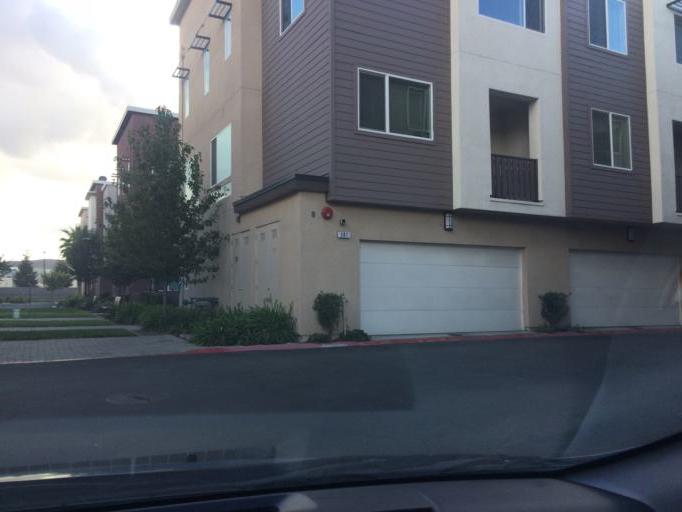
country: US
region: California
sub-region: Santa Clara County
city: Seven Trees
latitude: 37.2507
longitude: -121.7973
